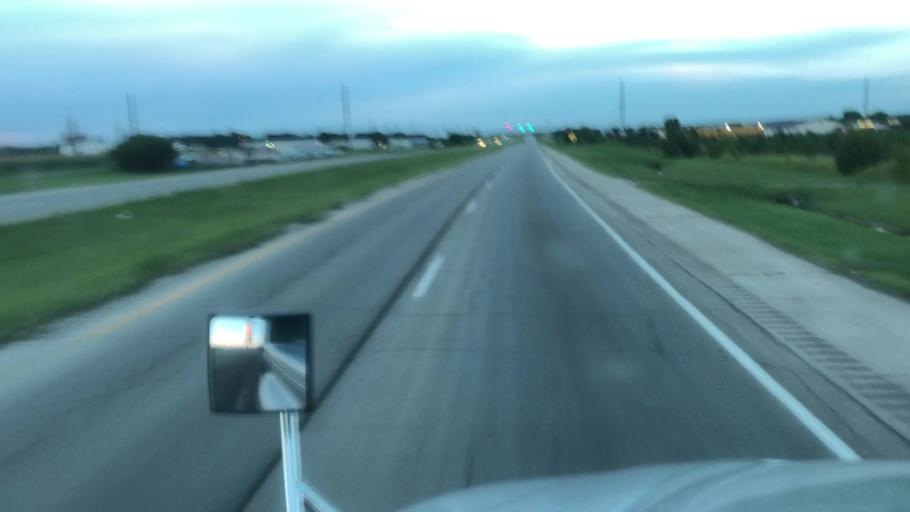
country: US
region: Oklahoma
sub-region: Kay County
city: Ponca City
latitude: 36.7504
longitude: -97.0667
